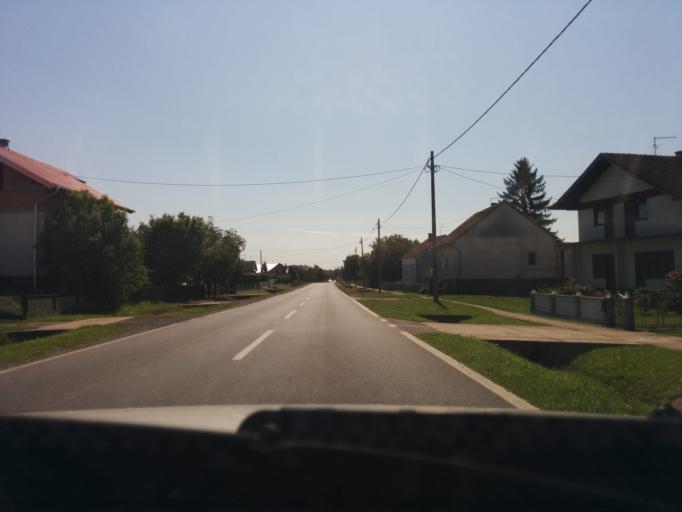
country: HR
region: Sisacko-Moslavacka
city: Lipovljani
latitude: 45.3701
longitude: 16.9253
